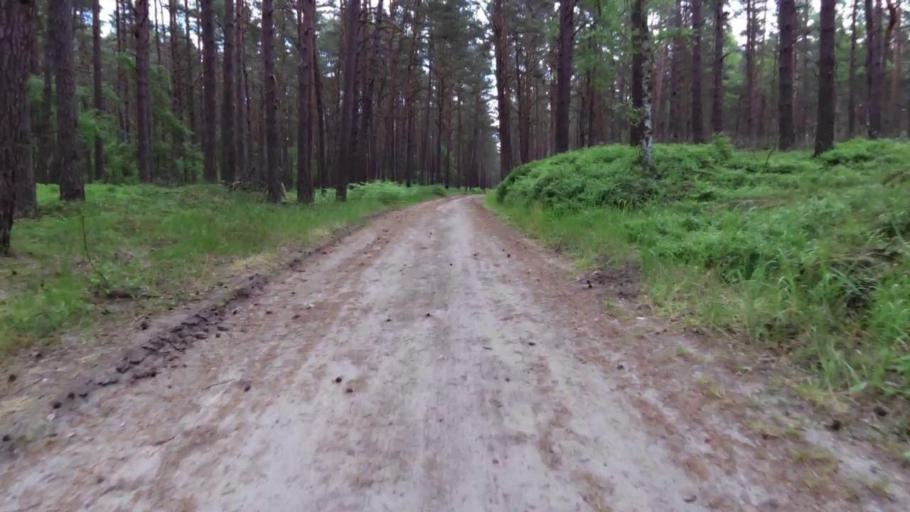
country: PL
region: West Pomeranian Voivodeship
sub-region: Swinoujscie
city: Swinoujscie
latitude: 53.9027
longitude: 14.3480
